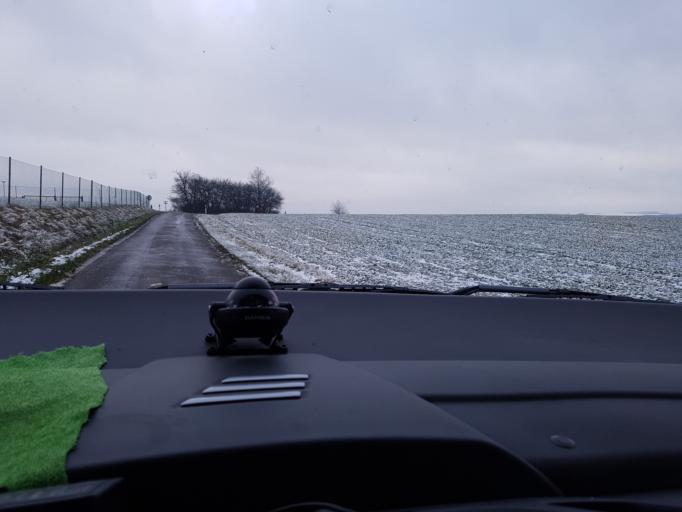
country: FR
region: Champagne-Ardenne
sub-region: Departement des Ardennes
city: Rimogne
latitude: 49.7959
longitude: 4.4356
